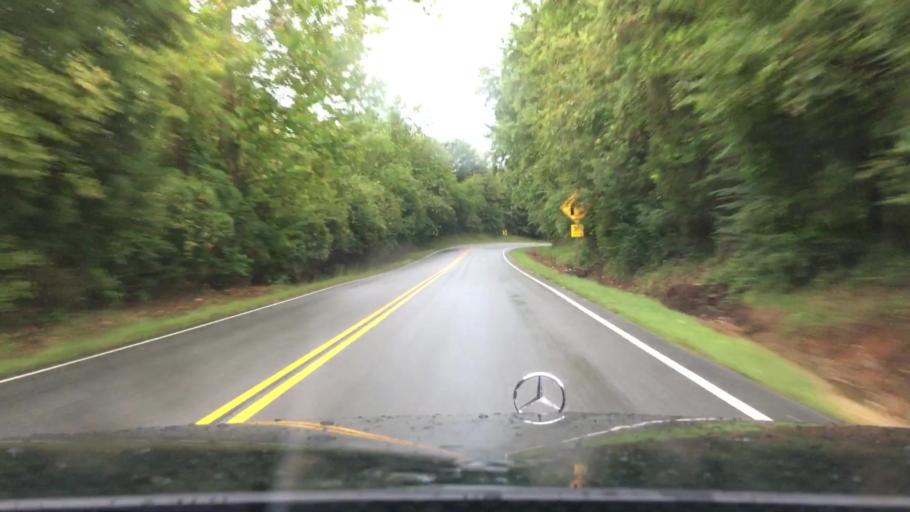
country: US
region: Virginia
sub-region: Amherst County
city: Amherst
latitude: 37.7102
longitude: -79.0231
